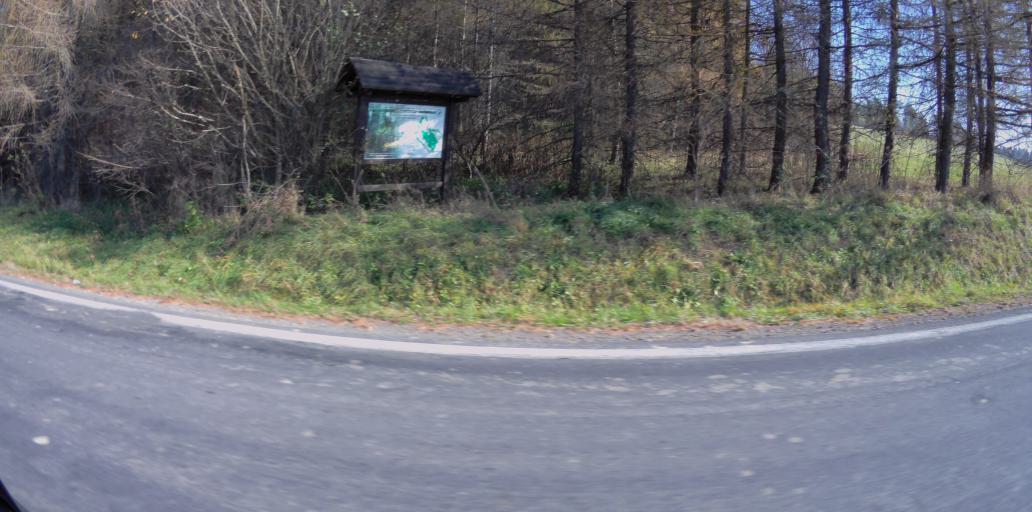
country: PL
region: Subcarpathian Voivodeship
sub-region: Powiat bieszczadzki
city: Ustrzyki Dolne
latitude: 49.5172
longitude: 22.6059
